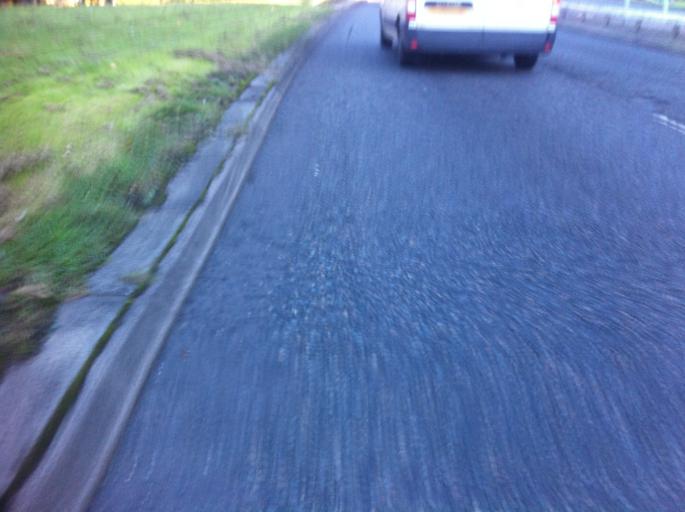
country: GB
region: Scotland
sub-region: Glasgow City
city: Glasgow
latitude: 55.8809
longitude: -4.2342
